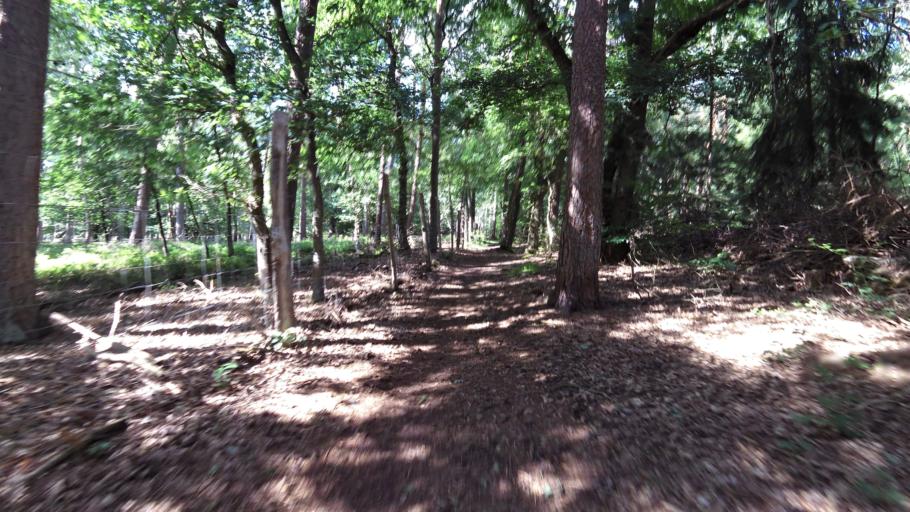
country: NL
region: Gelderland
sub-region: Gemeente Epe
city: Vaassen
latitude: 52.2737
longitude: 5.9223
